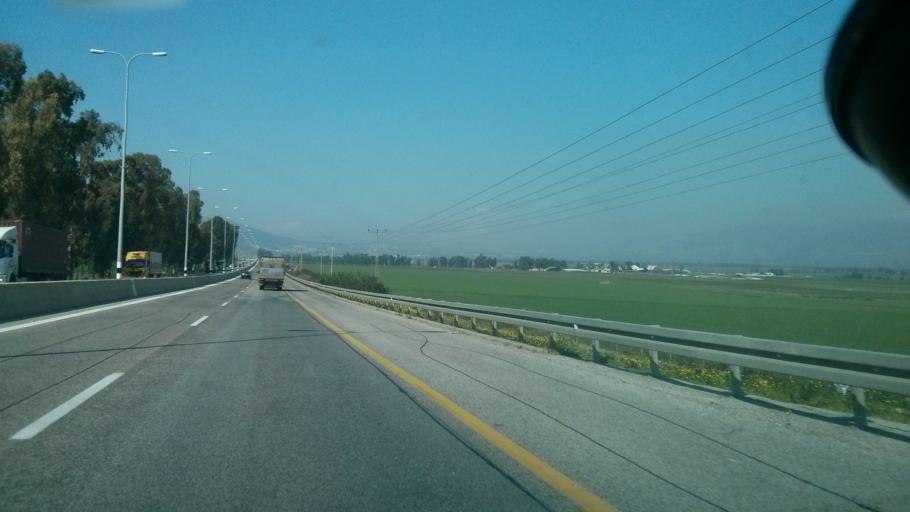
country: IL
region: Northern District
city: Qiryat Shemona
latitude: 33.0944
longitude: 35.5750
